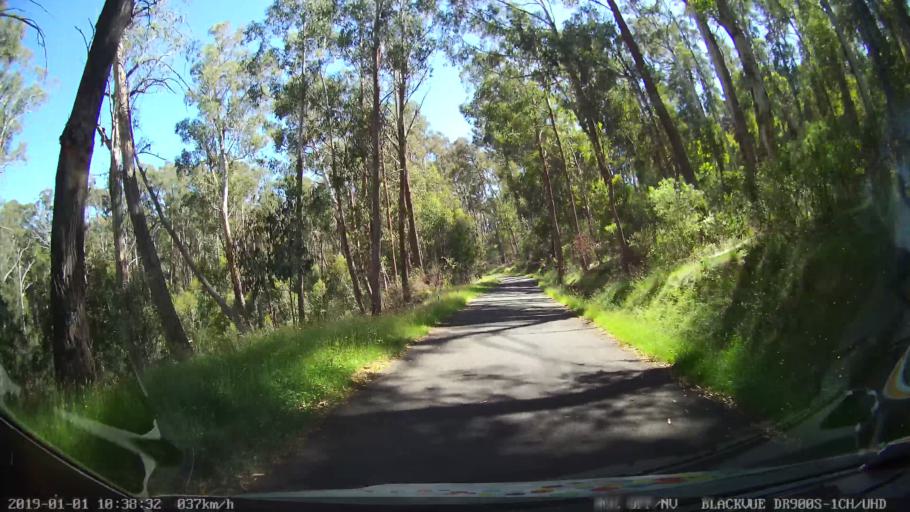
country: AU
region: New South Wales
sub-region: Snowy River
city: Jindabyne
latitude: -36.0448
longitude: 148.3007
